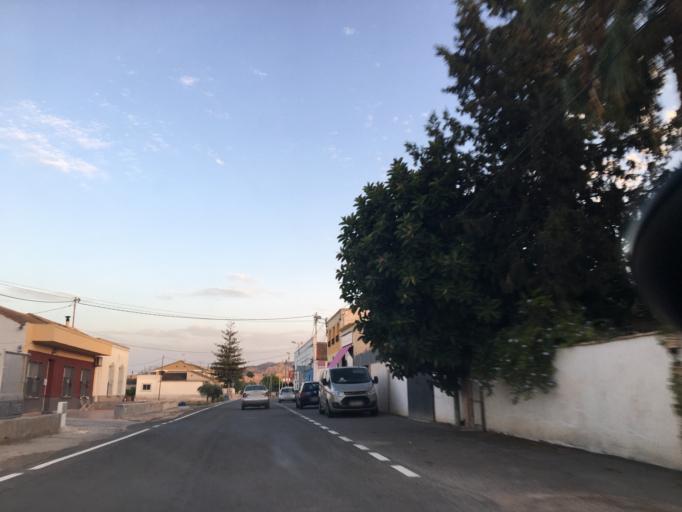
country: ES
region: Murcia
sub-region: Murcia
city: Santomera
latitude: 38.0293
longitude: -1.0587
